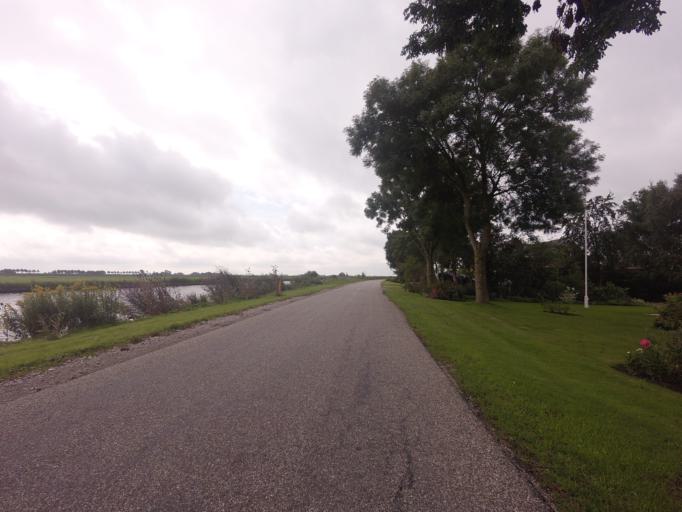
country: NL
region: Friesland
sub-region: Sudwest Fryslan
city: Workum
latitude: 52.9926
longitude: 5.4744
